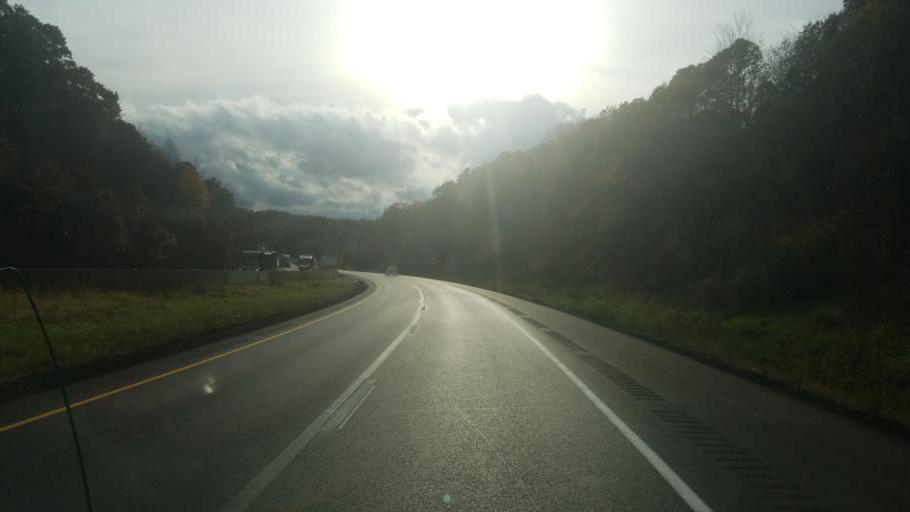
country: US
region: Pennsylvania
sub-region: Clarion County
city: Knox
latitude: 41.1788
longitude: -79.6936
